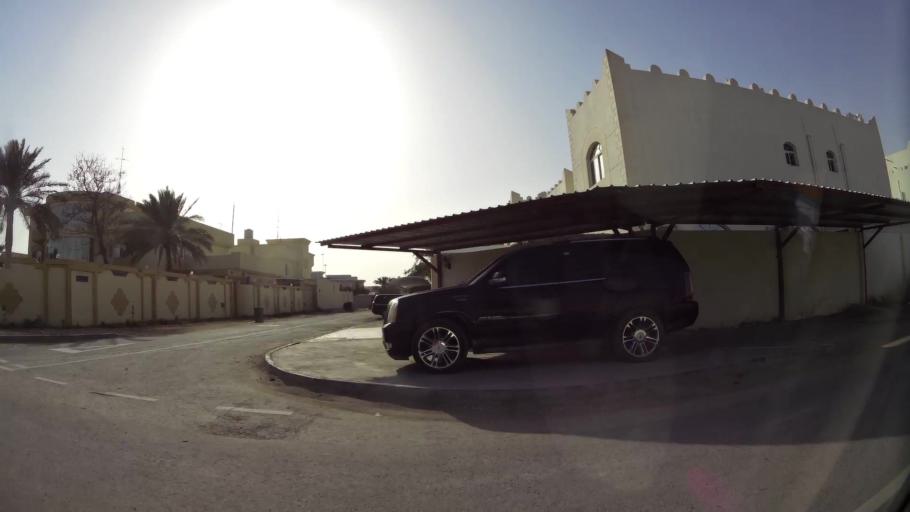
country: QA
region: Baladiyat ar Rayyan
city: Ar Rayyan
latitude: 25.3299
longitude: 51.4287
